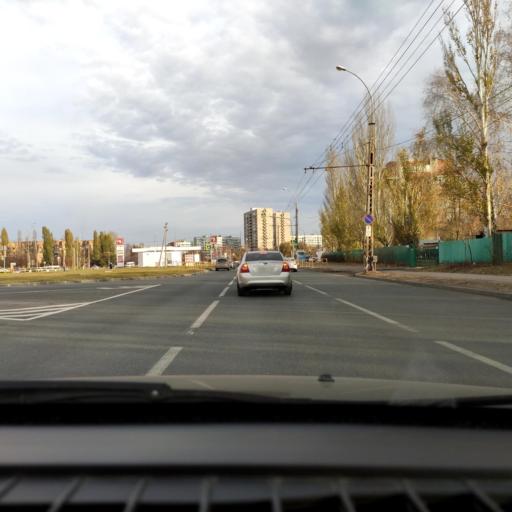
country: RU
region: Samara
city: Tol'yatti
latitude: 53.5149
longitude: 49.3082
